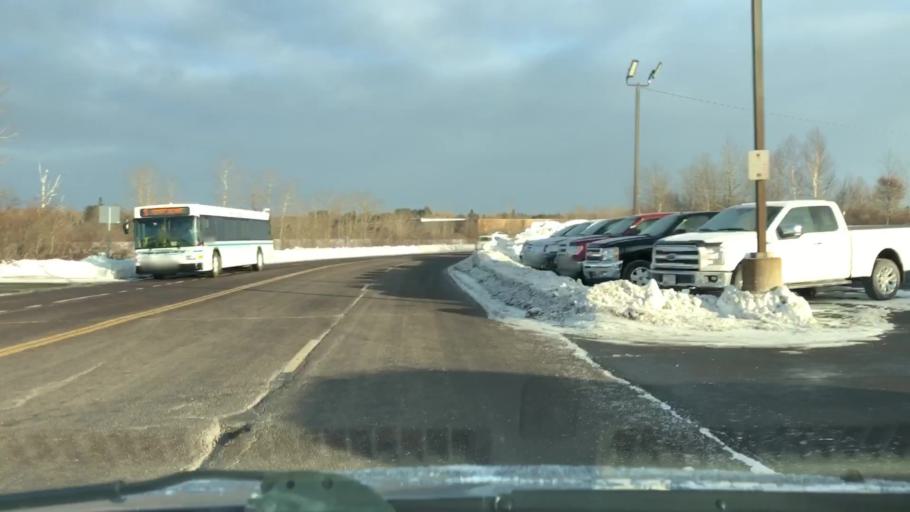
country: US
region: Minnesota
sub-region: Saint Louis County
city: Hermantown
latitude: 46.8129
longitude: -92.1736
